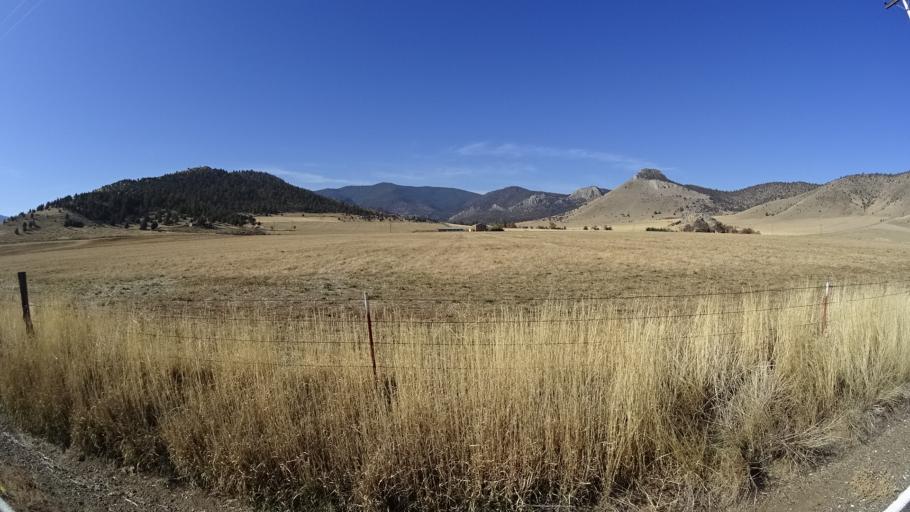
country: US
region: California
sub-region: Siskiyou County
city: Weed
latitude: 41.5000
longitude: -122.5503
